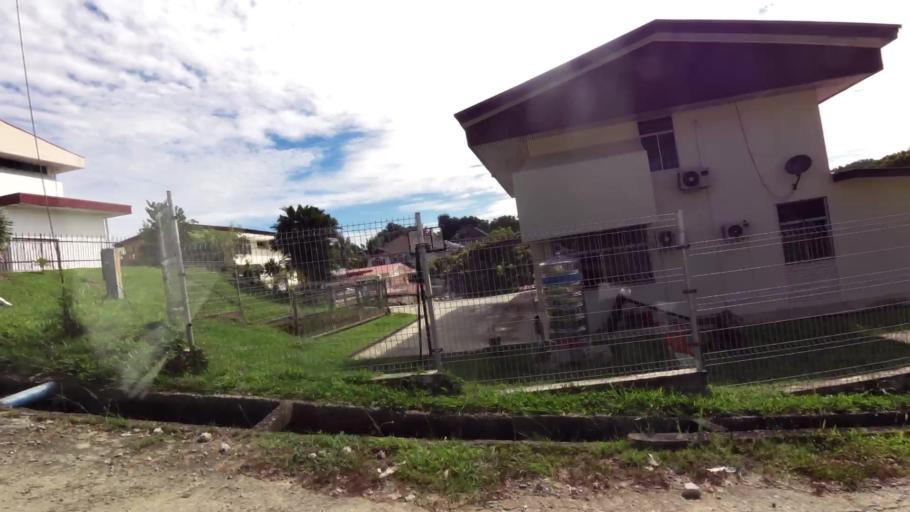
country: BN
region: Brunei and Muara
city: Bandar Seri Begawan
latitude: 4.9055
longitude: 114.9780
